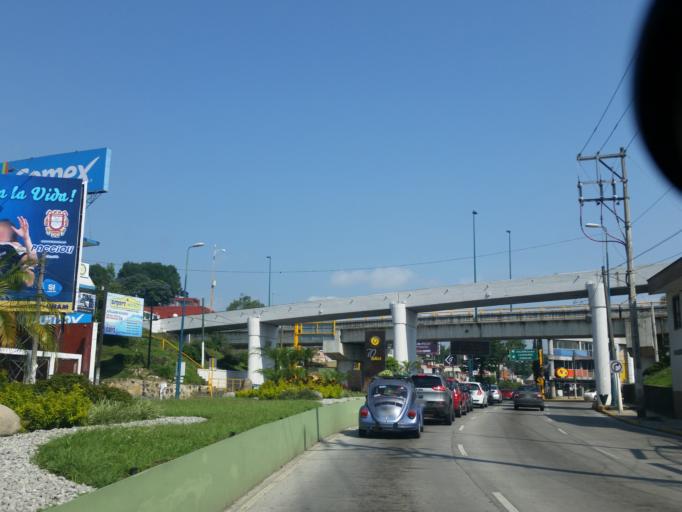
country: MX
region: Veracruz
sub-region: Xalapa
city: Xalapa de Enriquez
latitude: 19.5219
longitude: -96.9098
